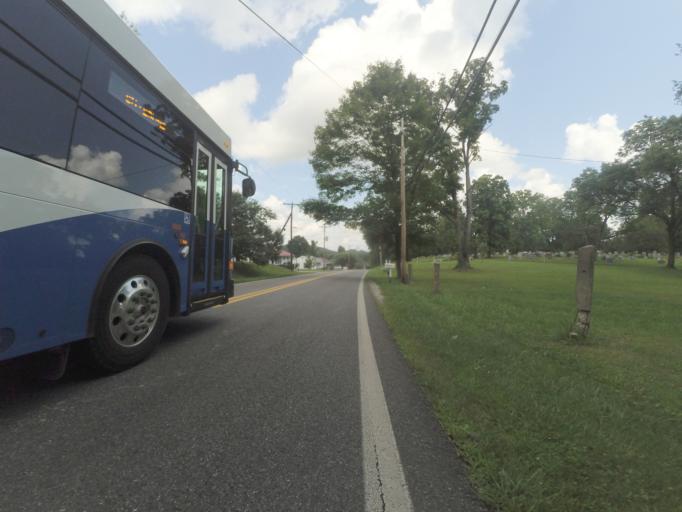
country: US
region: West Virginia
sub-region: Cabell County
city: Pea Ridge
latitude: 38.4180
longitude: -82.3094
